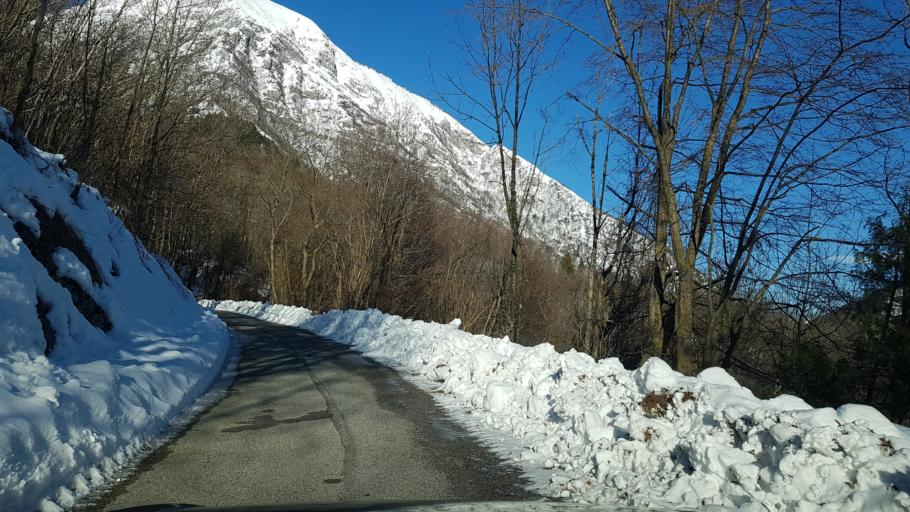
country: IT
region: Friuli Venezia Giulia
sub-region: Provincia di Udine
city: Forgaria nel Friuli
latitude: 46.2628
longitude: 12.9954
